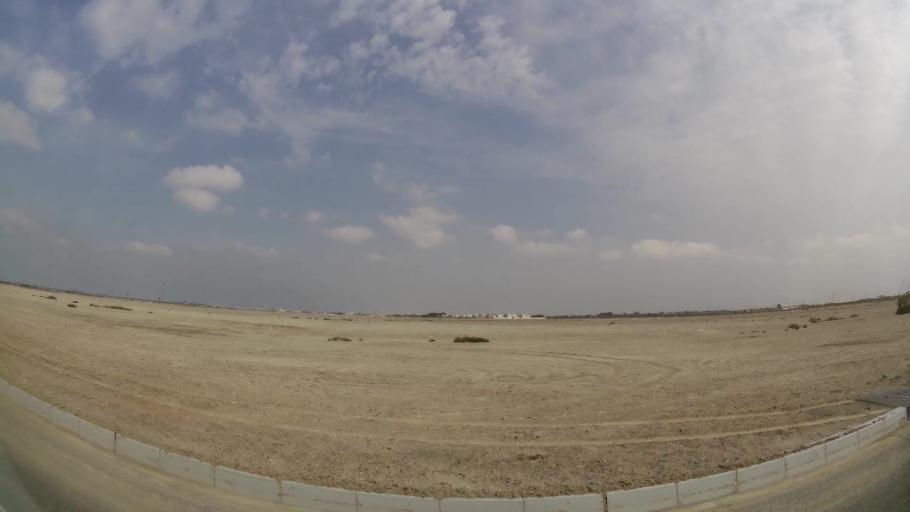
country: AE
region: Abu Dhabi
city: Abu Dhabi
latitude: 24.5784
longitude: 54.6453
